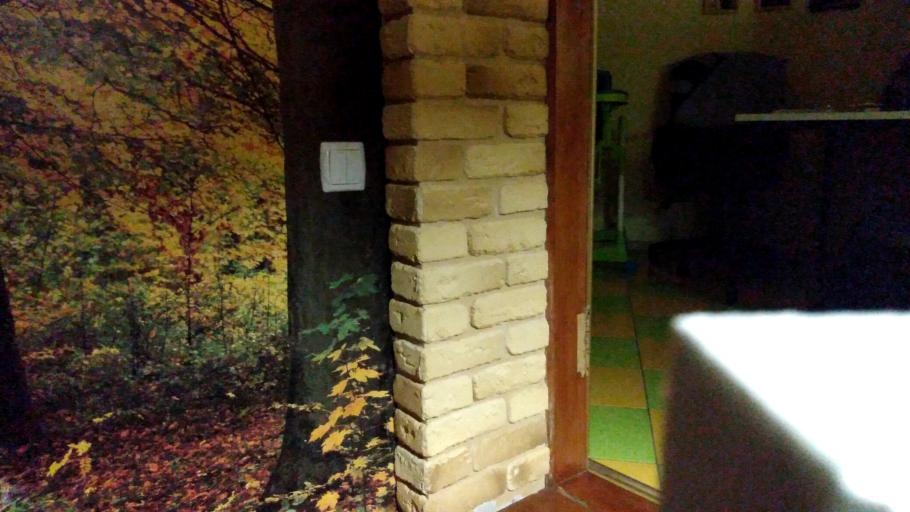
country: RU
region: Vologda
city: Lipin Bor
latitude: 60.7898
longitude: 38.0368
